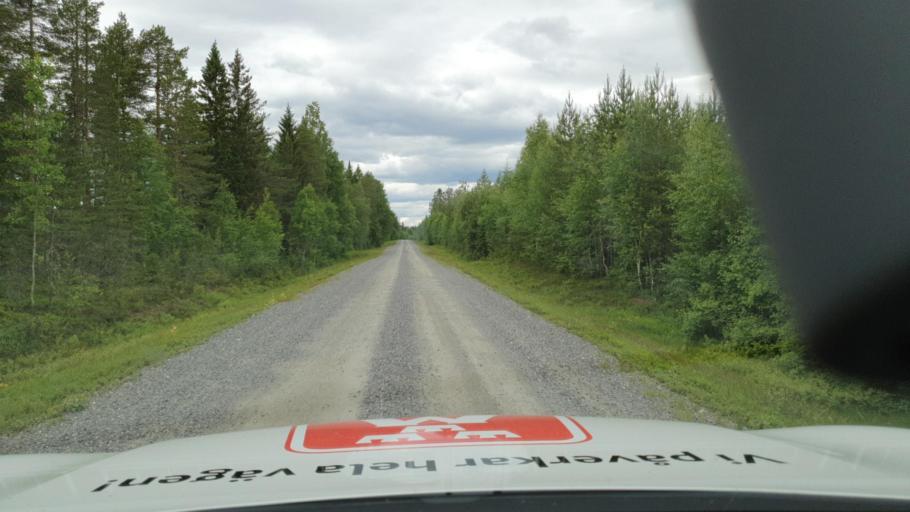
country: SE
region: Vaesterbotten
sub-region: Nordmalings Kommun
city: Nordmaling
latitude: 63.7441
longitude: 19.3827
